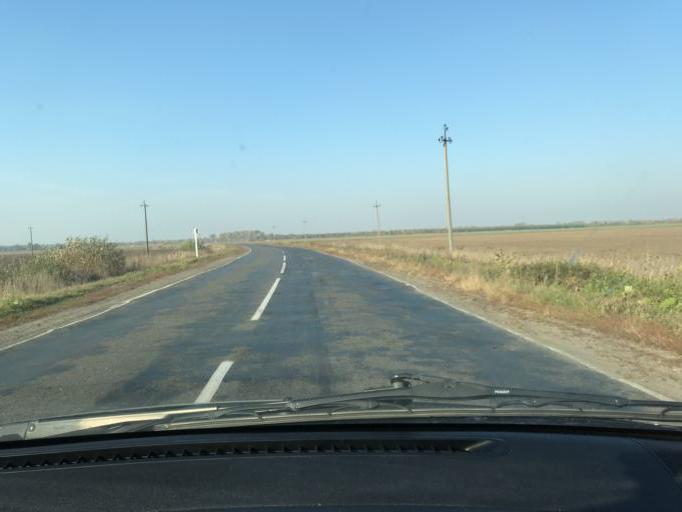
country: BY
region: Brest
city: Davyd-Haradok
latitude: 52.0644
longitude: 27.2539
